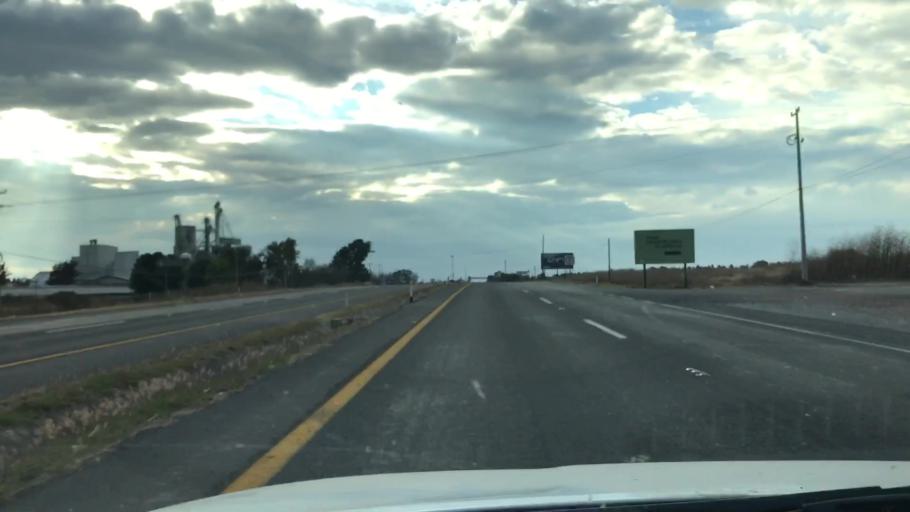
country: MX
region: Guanajuato
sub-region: Penjamo
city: Mezquite de Luna
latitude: 20.3810
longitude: -101.8214
